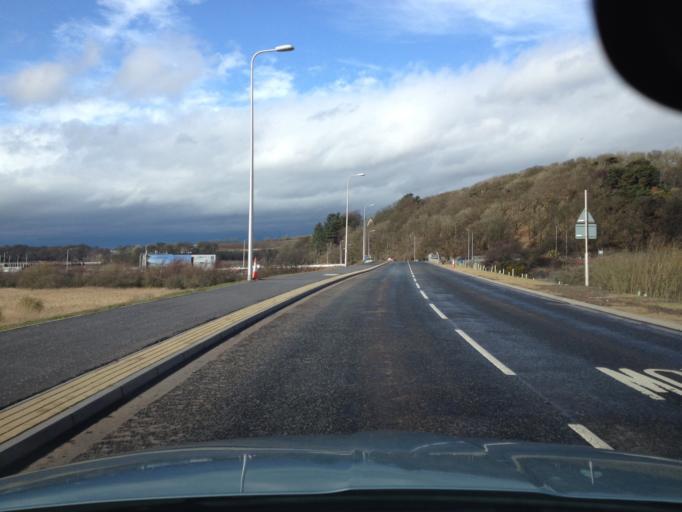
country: GB
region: Scotland
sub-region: Fife
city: Inverkeithing
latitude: 56.0191
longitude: -3.4119
